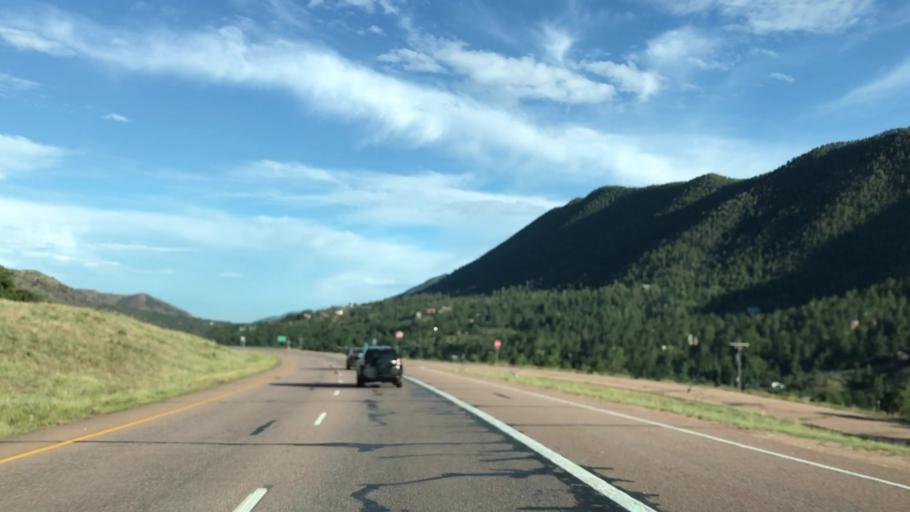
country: US
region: Colorado
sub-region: El Paso County
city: Cascade-Chipita Park
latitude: 38.9266
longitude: -104.9981
